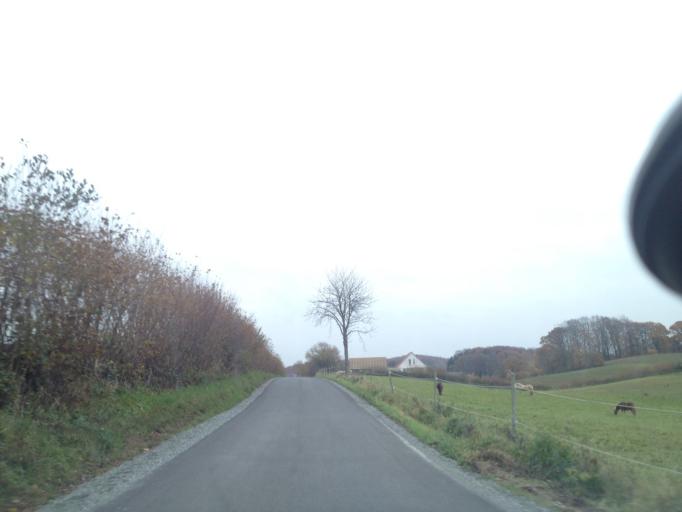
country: DK
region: South Denmark
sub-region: Nordfyns Kommune
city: Sonderso
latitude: 55.4264
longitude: 10.2205
